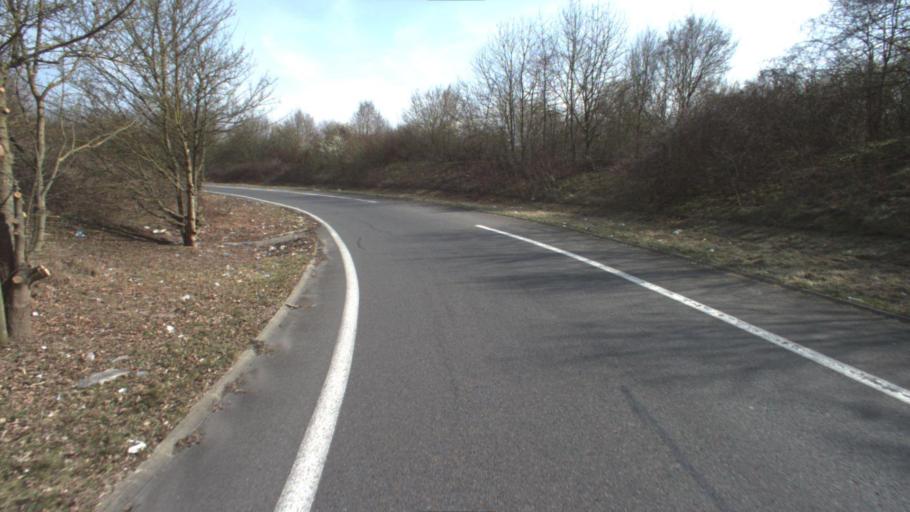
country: FR
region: Ile-de-France
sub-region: Departement de l'Essonne
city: Courcouronnes
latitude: 48.6256
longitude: 2.3989
